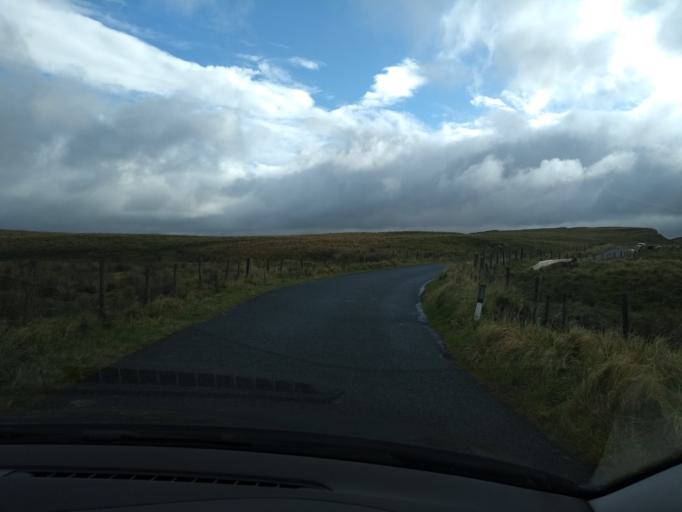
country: GB
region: England
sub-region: North Yorkshire
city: Settle
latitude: 54.0896
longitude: -2.1836
